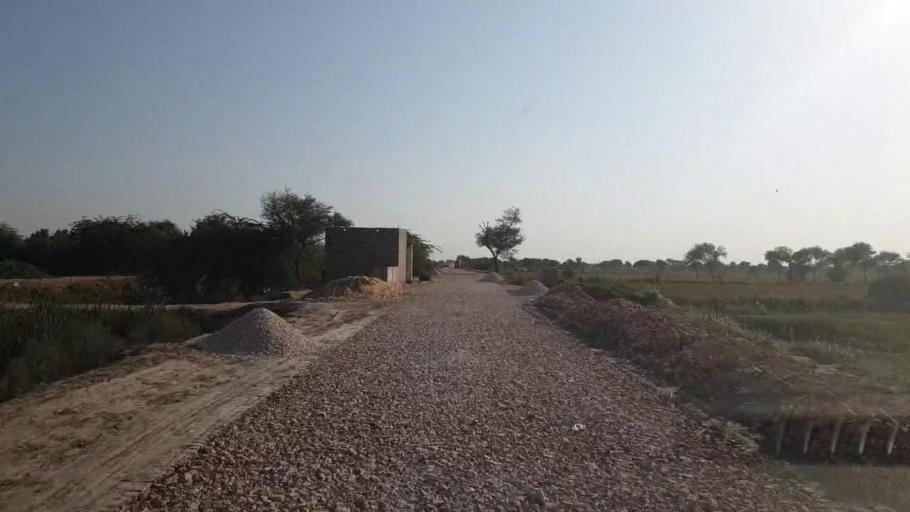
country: PK
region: Sindh
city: Talhar
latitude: 24.9336
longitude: 68.7499
